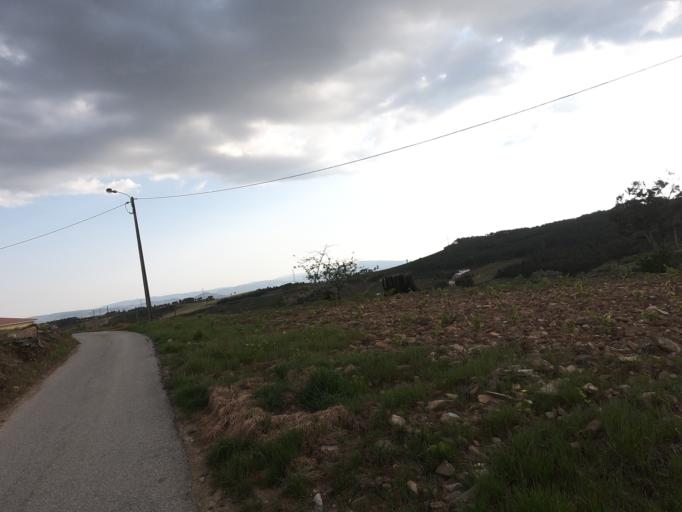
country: PT
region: Vila Real
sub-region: Sabrosa
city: Vilela
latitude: 41.2131
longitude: -7.6642
